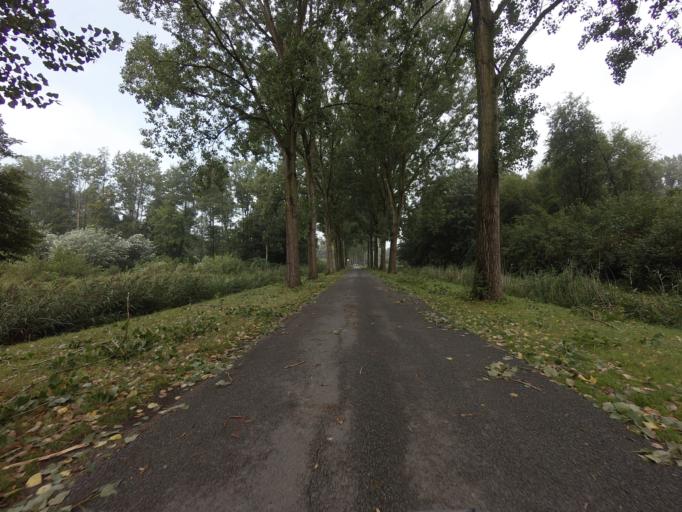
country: NL
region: North Holland
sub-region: Gemeente Huizen
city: Huizen
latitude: 52.3221
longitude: 5.2936
